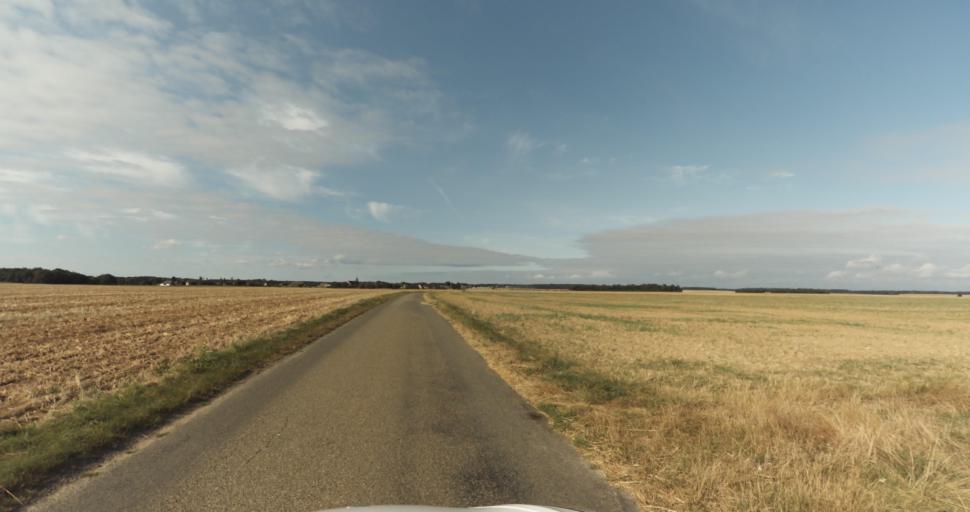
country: FR
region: Haute-Normandie
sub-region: Departement de l'Eure
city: Nonancourt
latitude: 48.8127
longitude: 1.1492
